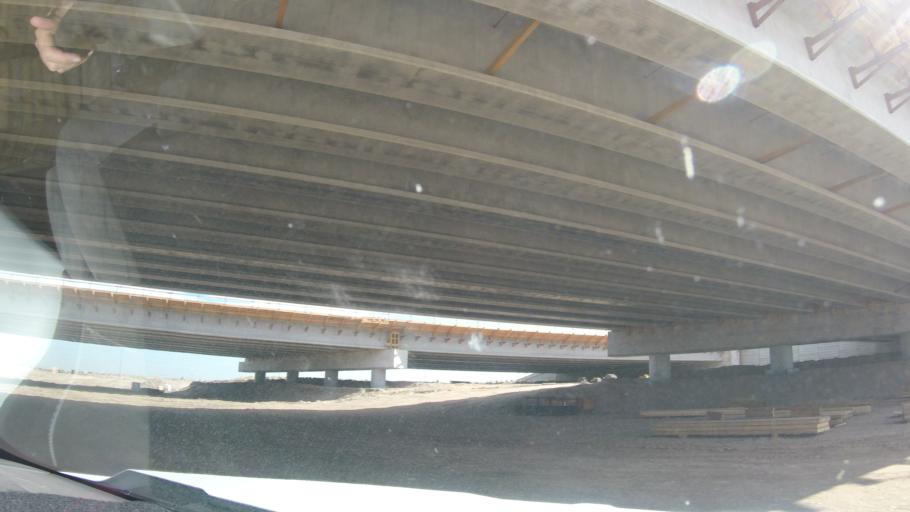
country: US
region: Arizona
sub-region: Maricopa County
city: Laveen
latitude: 33.3963
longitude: -112.1926
